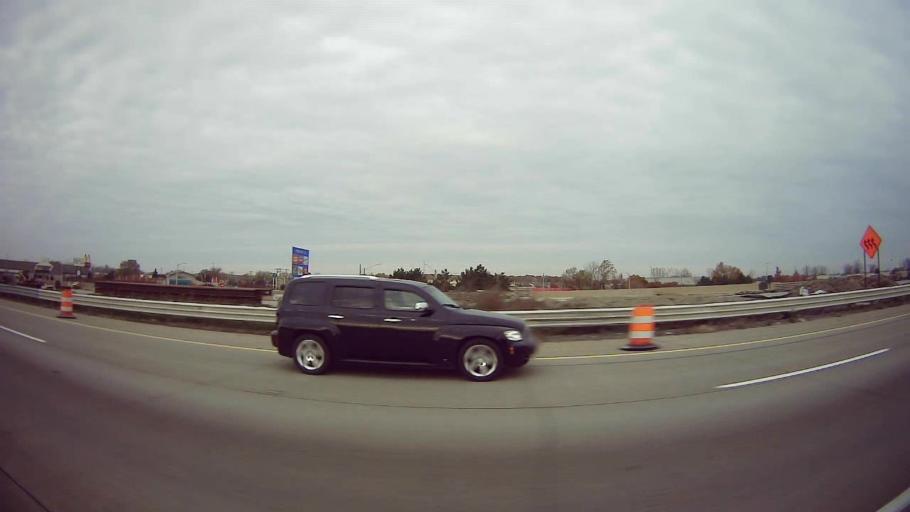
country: US
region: Michigan
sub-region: Wayne County
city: Southgate
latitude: 42.2126
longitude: -83.2230
